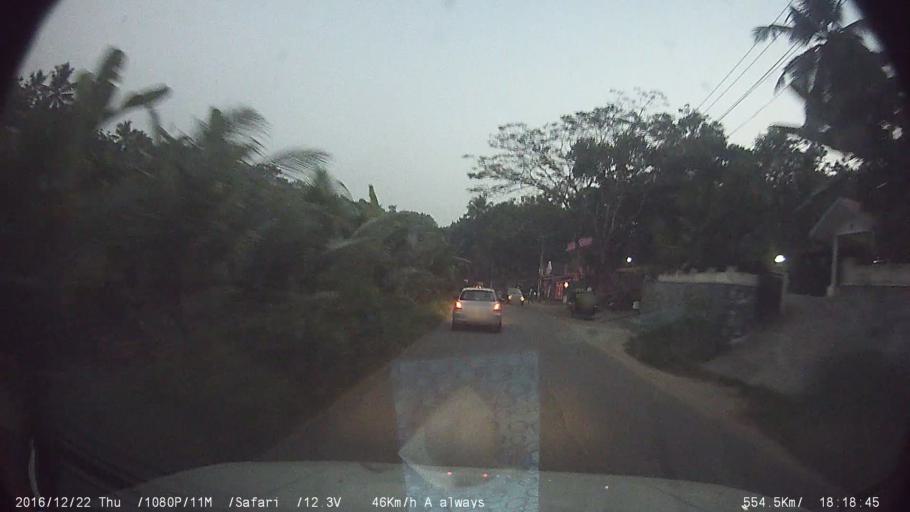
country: IN
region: Kerala
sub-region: Kottayam
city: Palackattumala
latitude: 9.7523
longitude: 76.6091
